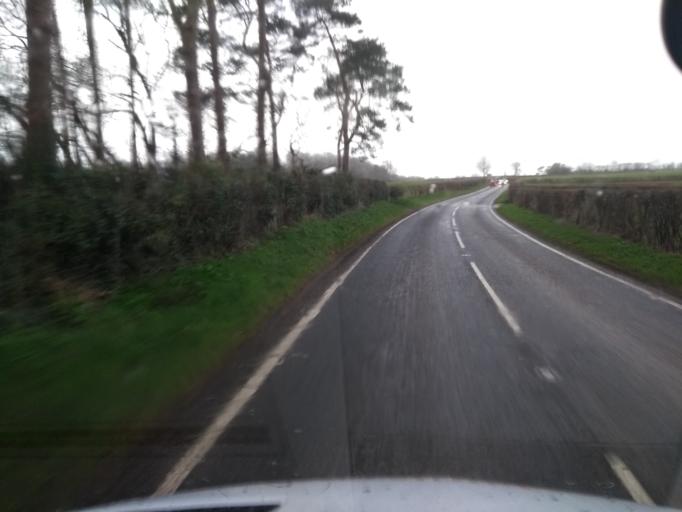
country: GB
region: England
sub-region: Somerset
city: Castle Cary
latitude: 51.0828
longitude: -2.4775
